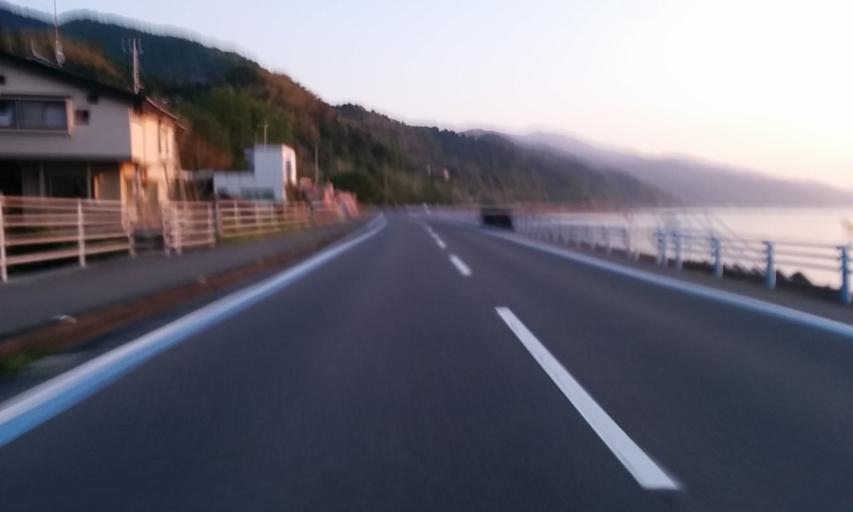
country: JP
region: Ehime
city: Iyo
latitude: 33.6712
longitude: 132.6112
